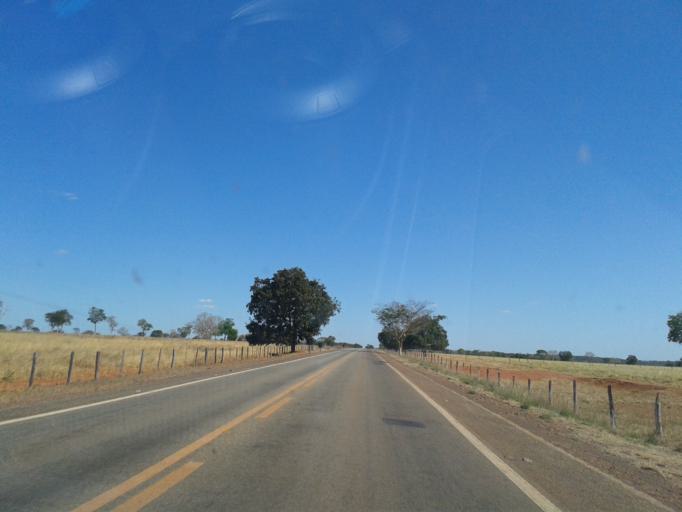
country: BR
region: Goias
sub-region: Crixas
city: Crixas
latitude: -14.1589
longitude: -50.3647
